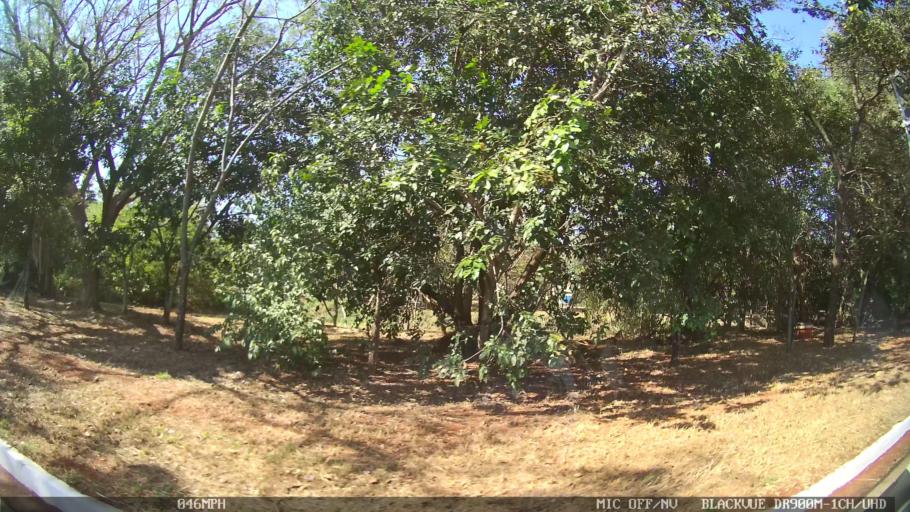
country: BR
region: Sao Paulo
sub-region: Ribeirao Preto
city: Ribeirao Preto
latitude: -21.2268
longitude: -47.7679
